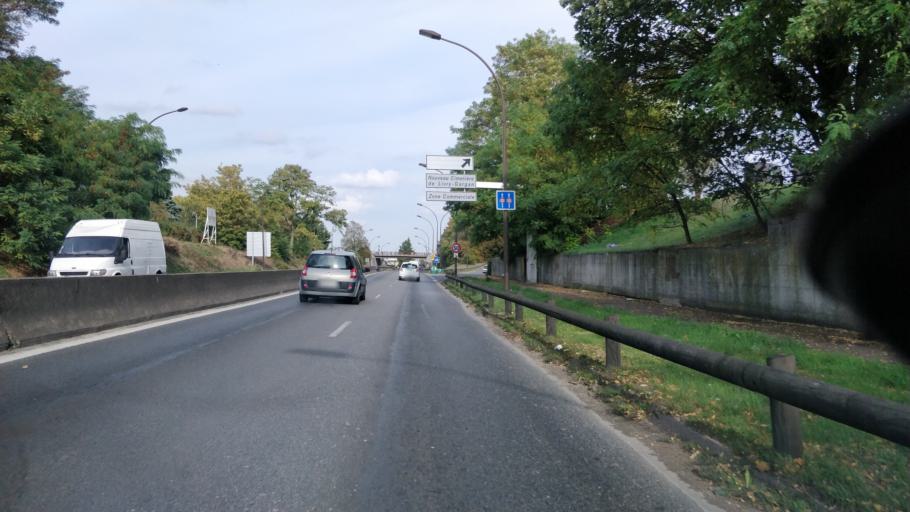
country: FR
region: Ile-de-France
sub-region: Departement de Seine-Saint-Denis
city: Livry-Gargan
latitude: 48.9276
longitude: 2.5514
